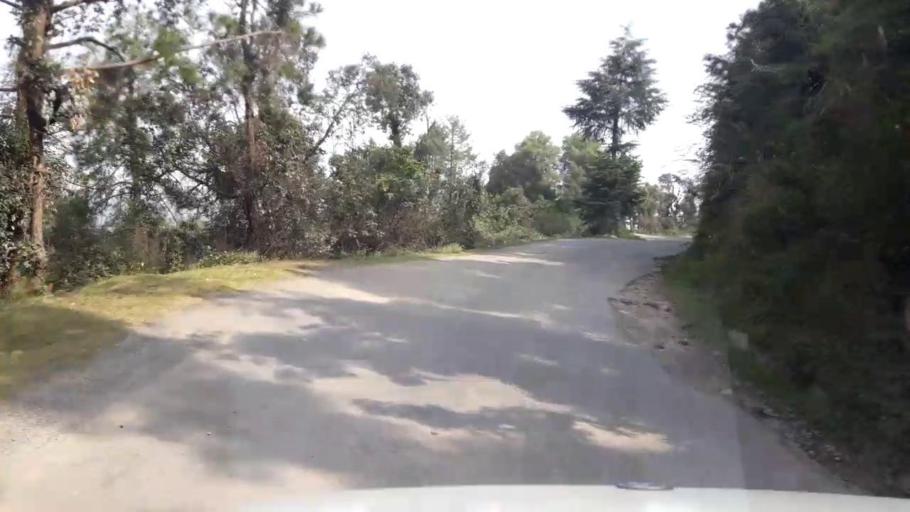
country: IN
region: Himachal Pradesh
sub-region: Shimla
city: Shimla
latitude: 31.0484
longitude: 77.1505
